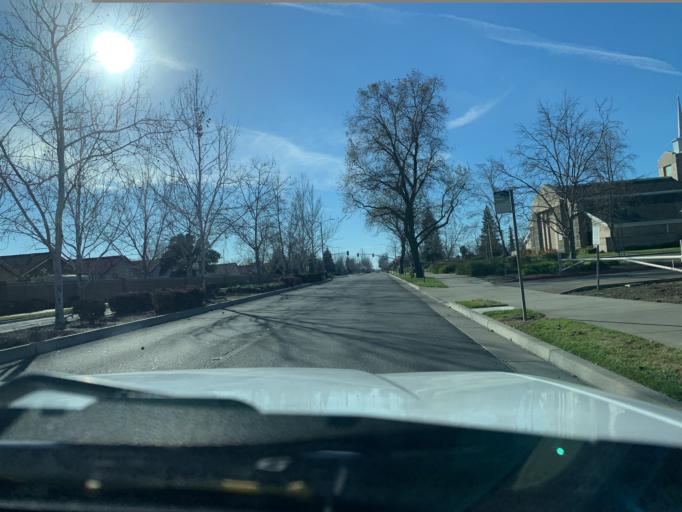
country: US
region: California
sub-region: Yolo County
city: Woodland
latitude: 38.6702
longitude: -121.7423
